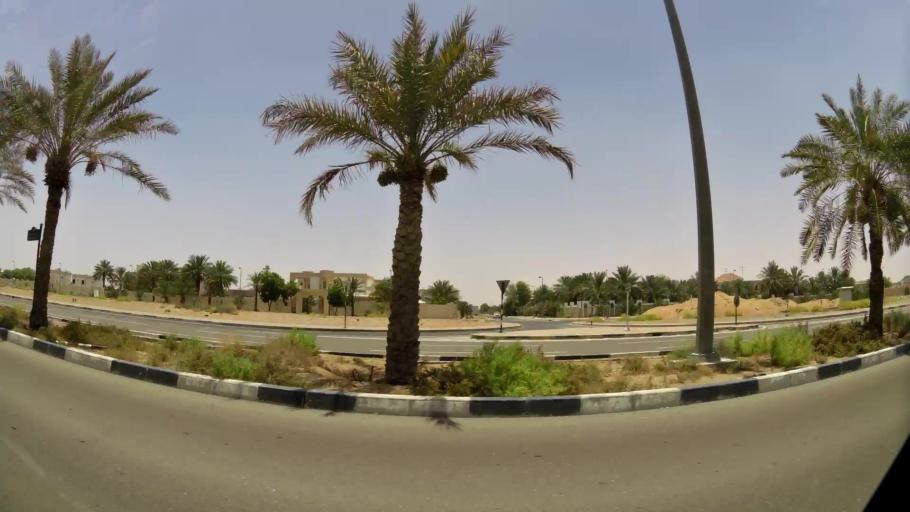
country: OM
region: Al Buraimi
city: Al Buraymi
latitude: 24.2636
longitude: 55.7204
